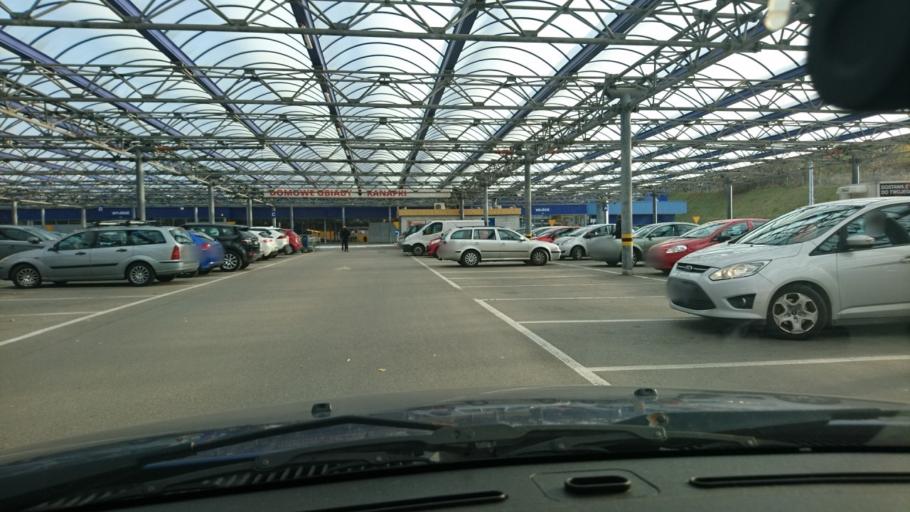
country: PL
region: Silesian Voivodeship
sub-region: Powiat bielski
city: Mazancowice
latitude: 49.8383
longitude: 19.0024
